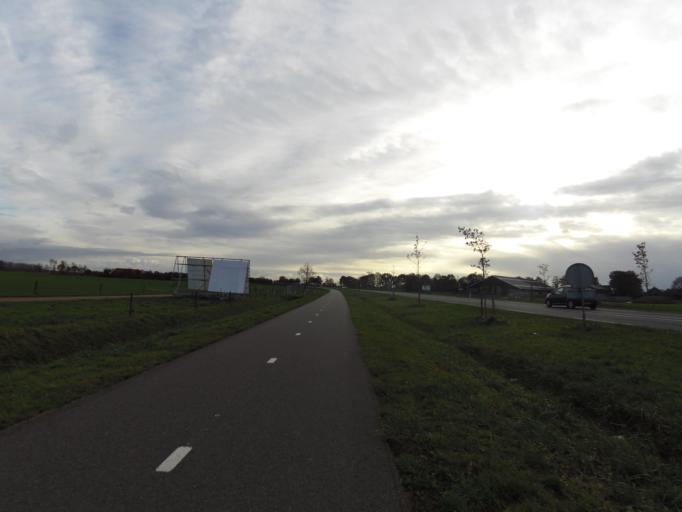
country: NL
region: Gelderland
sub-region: Gemeente Doetinchem
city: Doetinchem
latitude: 51.9335
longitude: 6.3149
